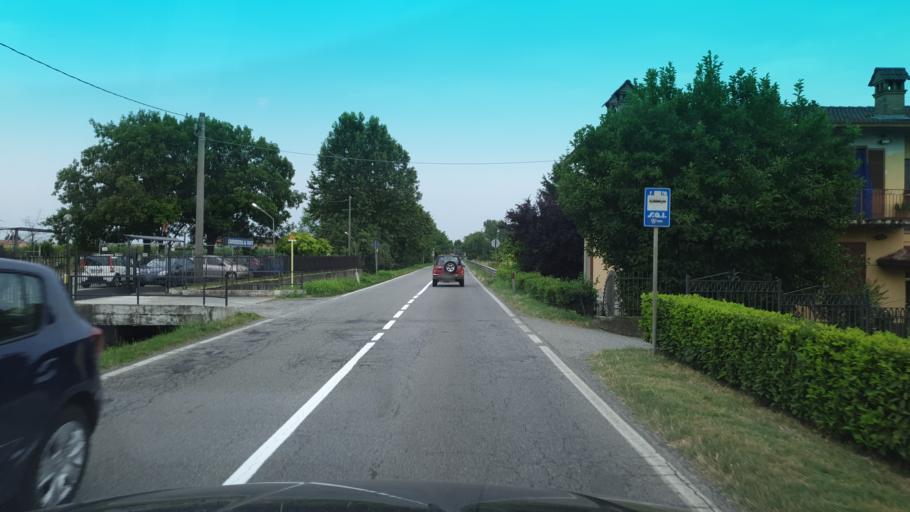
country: IT
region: Lombardy
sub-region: Provincia di Bergamo
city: Badalasco
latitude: 45.5331
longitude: 9.5380
